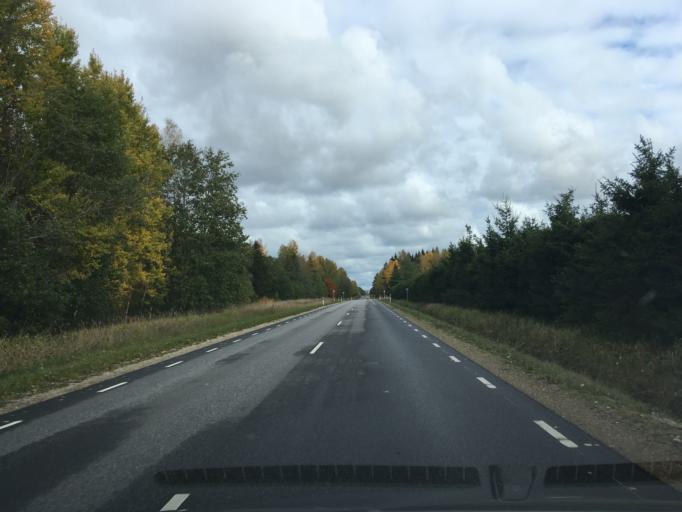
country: EE
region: Harju
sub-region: Anija vald
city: Kehra
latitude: 59.2323
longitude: 25.2827
